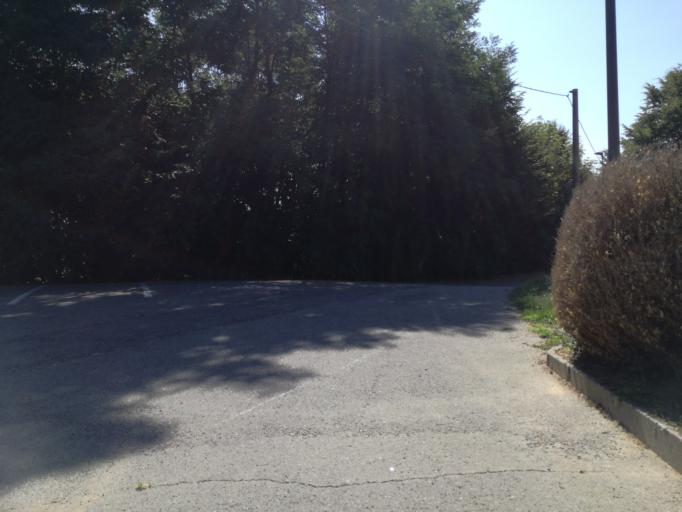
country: IT
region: Lombardy
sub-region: Provincia di Monza e Brianza
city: Porto d'Adda
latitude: 45.6656
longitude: 9.4753
